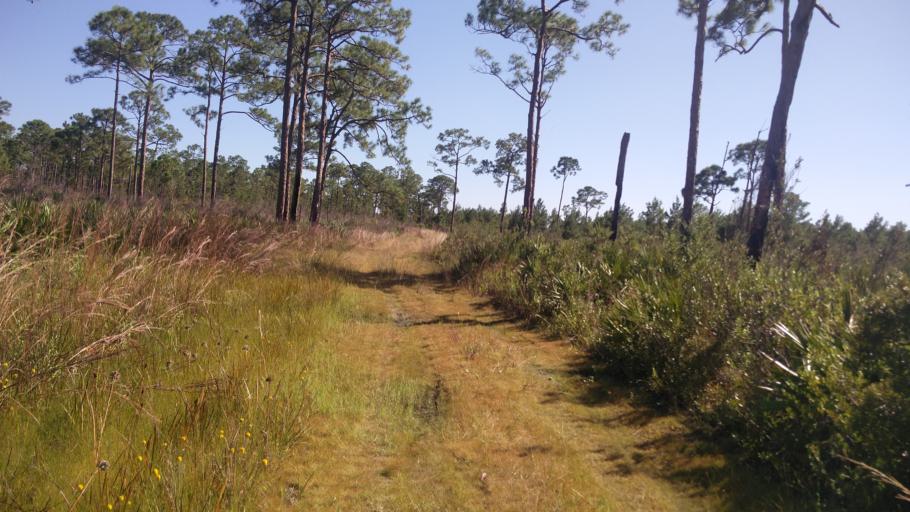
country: US
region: Florida
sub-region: Martin County
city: Hobe Sound
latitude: 27.0281
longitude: -80.1329
